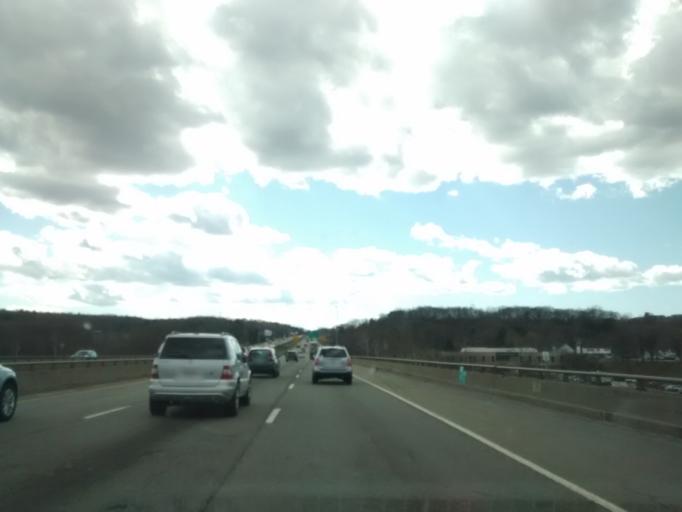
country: US
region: Massachusetts
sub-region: Worcester County
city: Hamilton
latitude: 42.2939
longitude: -71.7571
